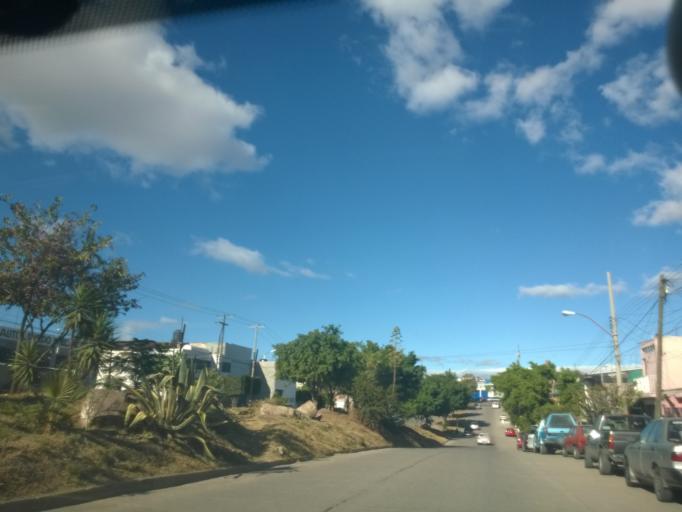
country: MX
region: Guanajuato
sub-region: Leon
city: Ejido la Joya
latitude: 21.1180
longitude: -101.7182
